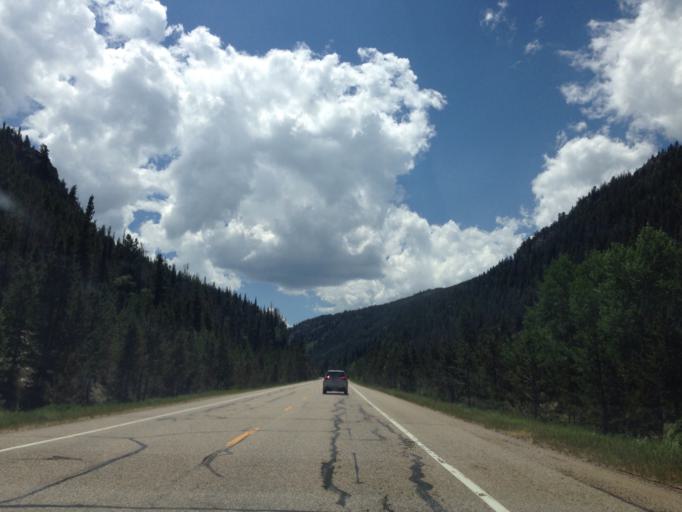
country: US
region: Colorado
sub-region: Larimer County
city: Estes Park
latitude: 40.6334
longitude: -105.8085
